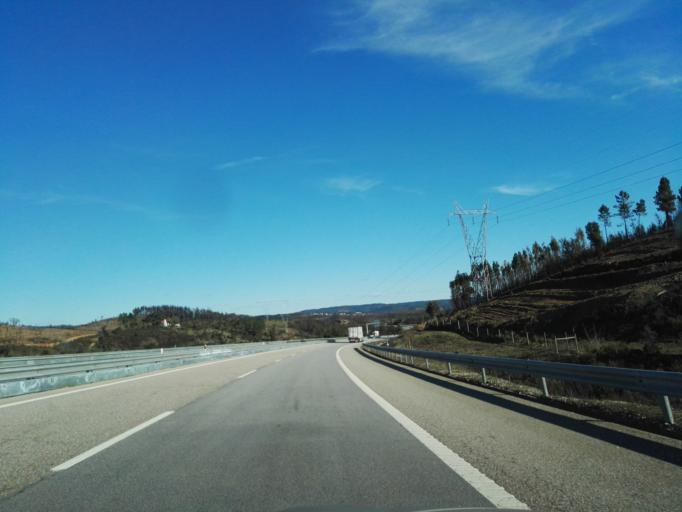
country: PT
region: Santarem
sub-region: Abrantes
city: Alferrarede
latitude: 39.4956
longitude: -8.0765
